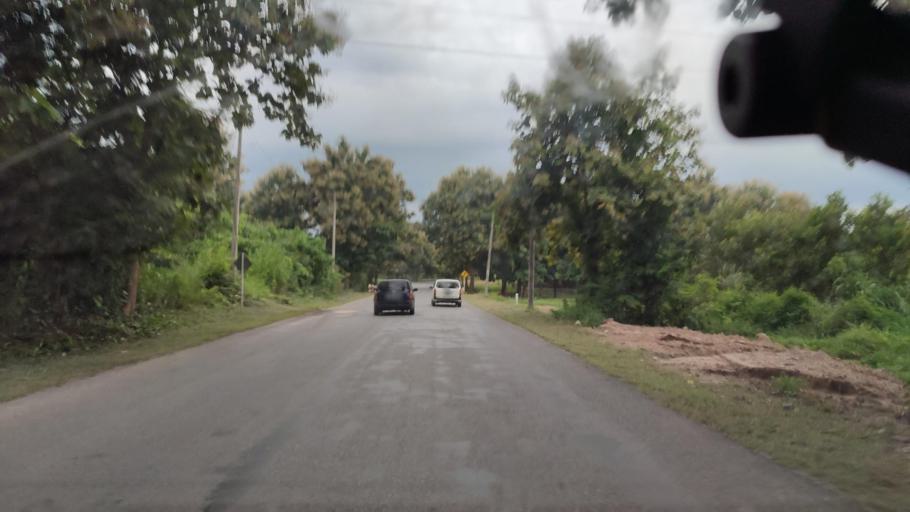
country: MM
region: Bago
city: Paungde
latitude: 18.5516
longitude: 95.2917
